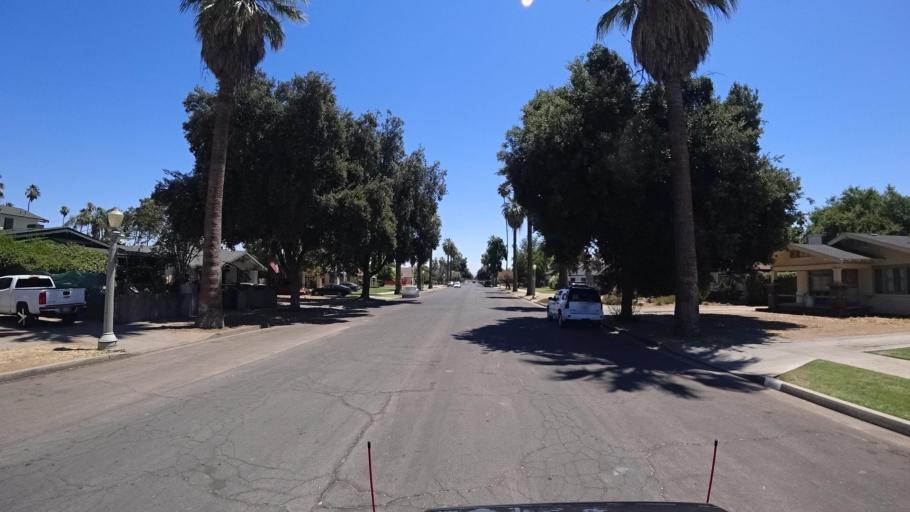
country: US
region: California
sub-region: Fresno County
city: Fresno
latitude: 36.7406
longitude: -119.7591
